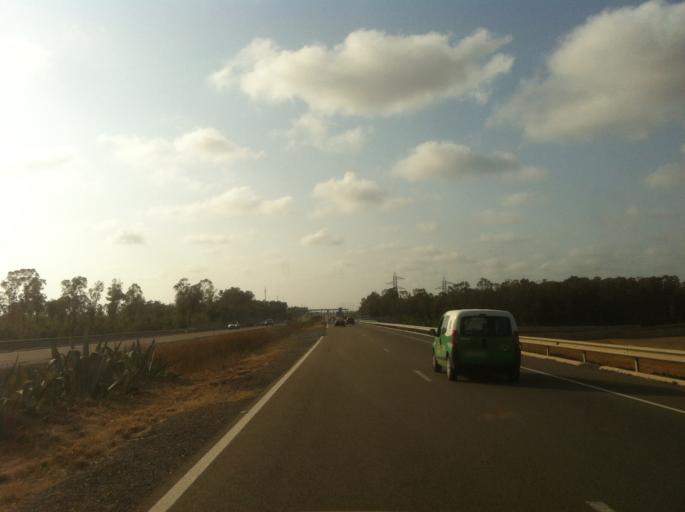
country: MA
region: Gharb-Chrarda-Beni Hssen
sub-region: Kenitra Province
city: Kenitra
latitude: 34.2240
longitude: -6.5329
